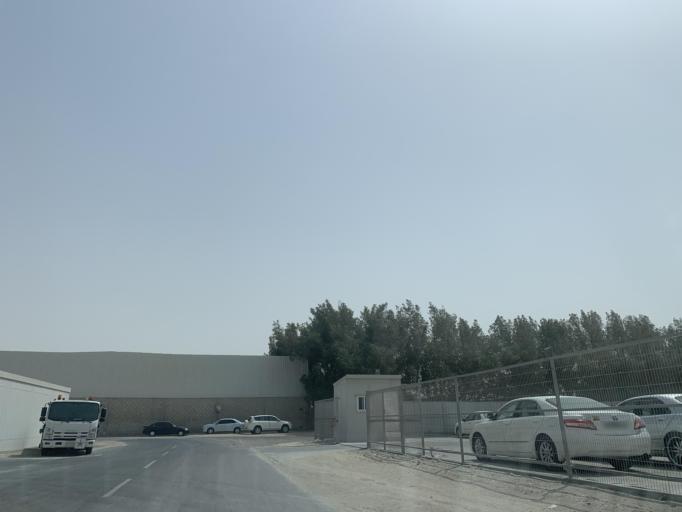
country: BH
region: Northern
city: Madinat `Isa
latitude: 26.1889
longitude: 50.5302
